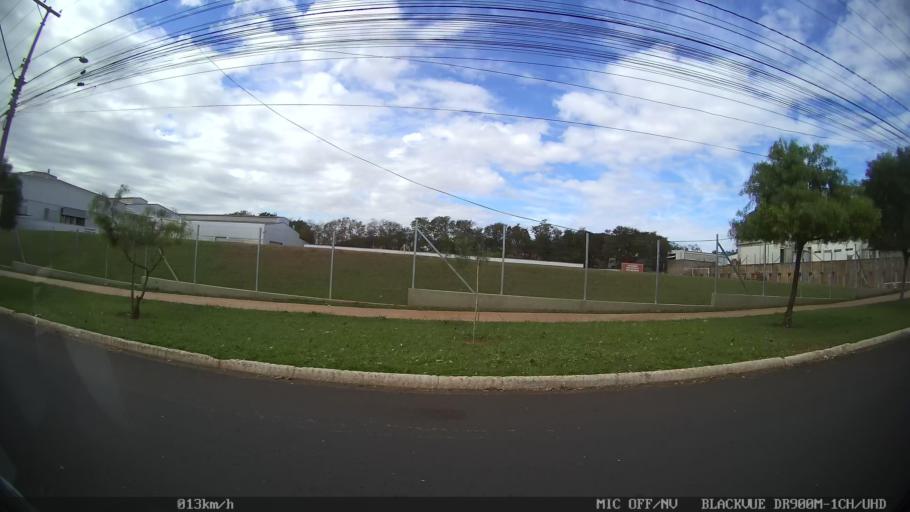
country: BR
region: Sao Paulo
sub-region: Sao Jose Do Rio Preto
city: Sao Jose do Rio Preto
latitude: -20.8066
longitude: -49.4910
